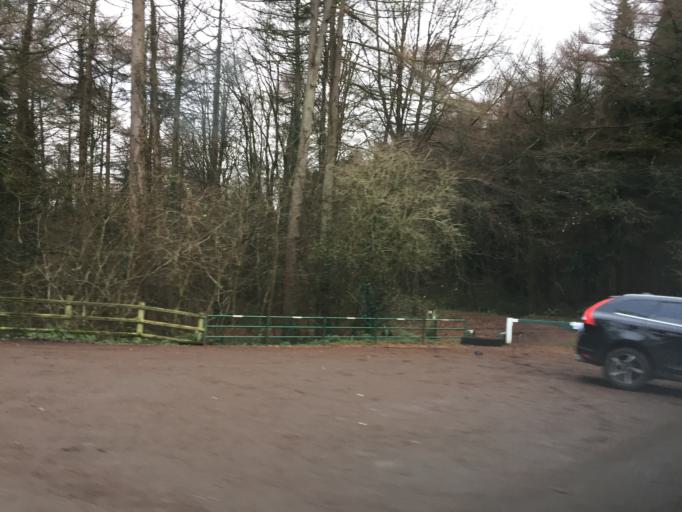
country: GB
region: Wales
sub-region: Monmouthshire
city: Rogiet
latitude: 51.6009
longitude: -2.7807
